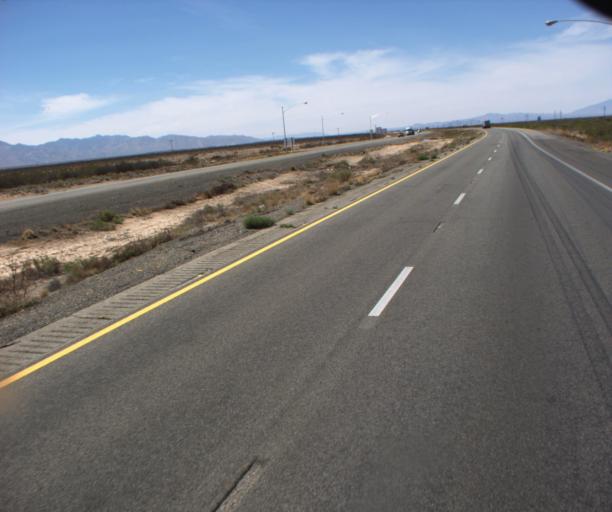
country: US
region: New Mexico
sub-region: Hidalgo County
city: Lordsburg
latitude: 32.2737
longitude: -109.2532
